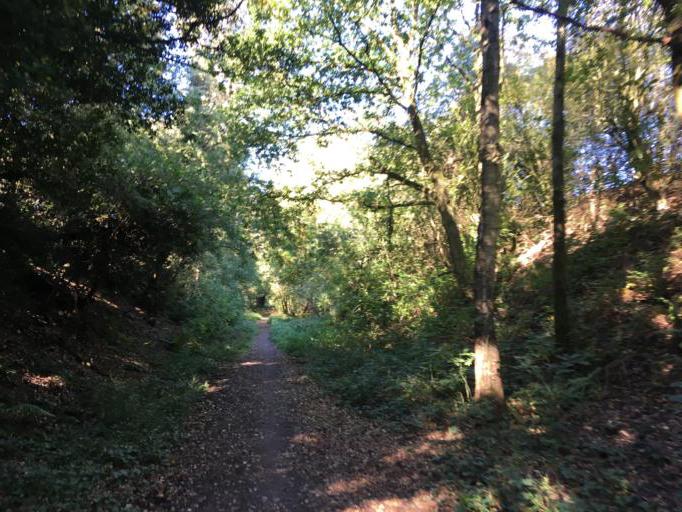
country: GB
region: England
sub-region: Solihull
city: Balsall Common
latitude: 52.3864
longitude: -1.6189
